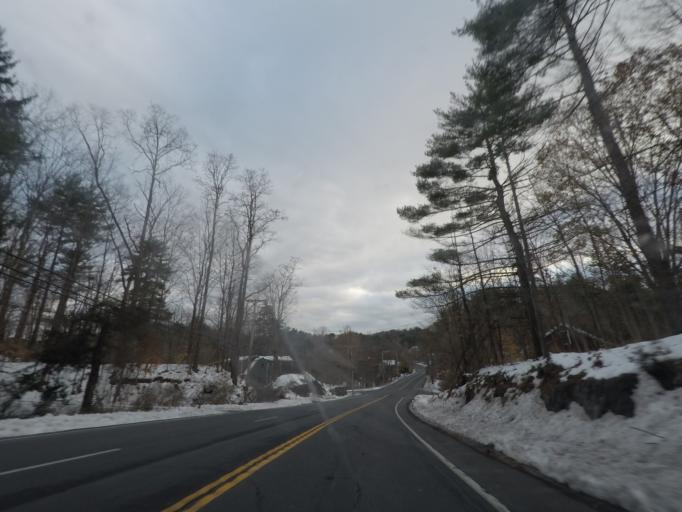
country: US
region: New York
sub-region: Ulster County
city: Hurley
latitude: 41.8882
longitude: -74.0429
